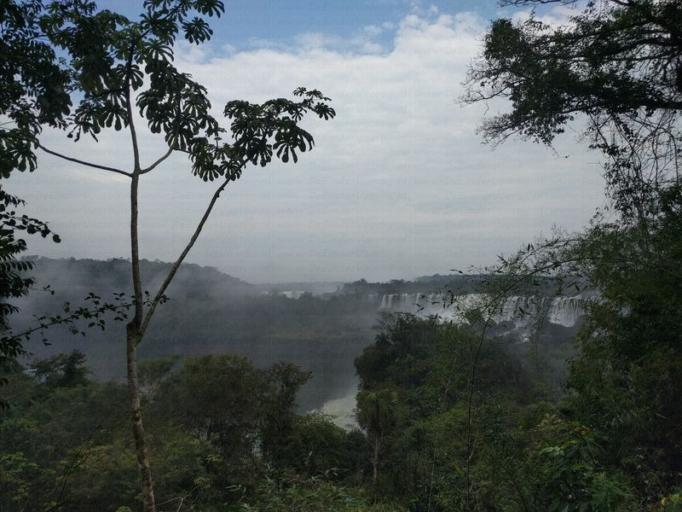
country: AR
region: Misiones
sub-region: Departamento de Iguazu
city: Puerto Iguazu
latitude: -25.6850
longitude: -54.4461
